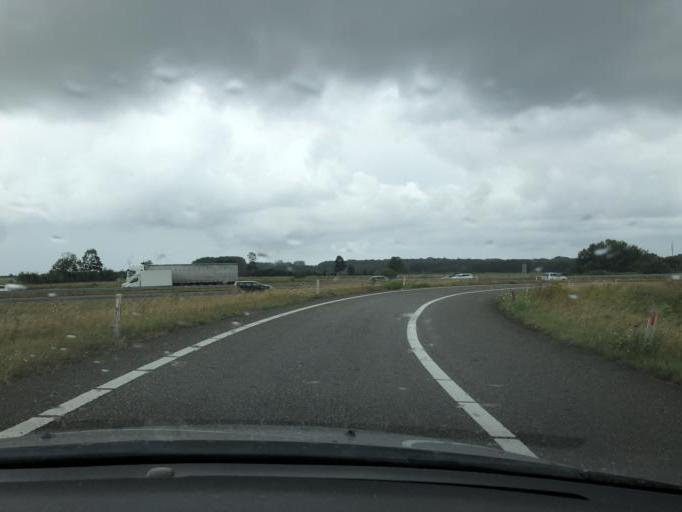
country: NL
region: North Brabant
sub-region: Gemeente Woensdrecht
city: Woensdrecht
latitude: 51.4395
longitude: 4.3093
